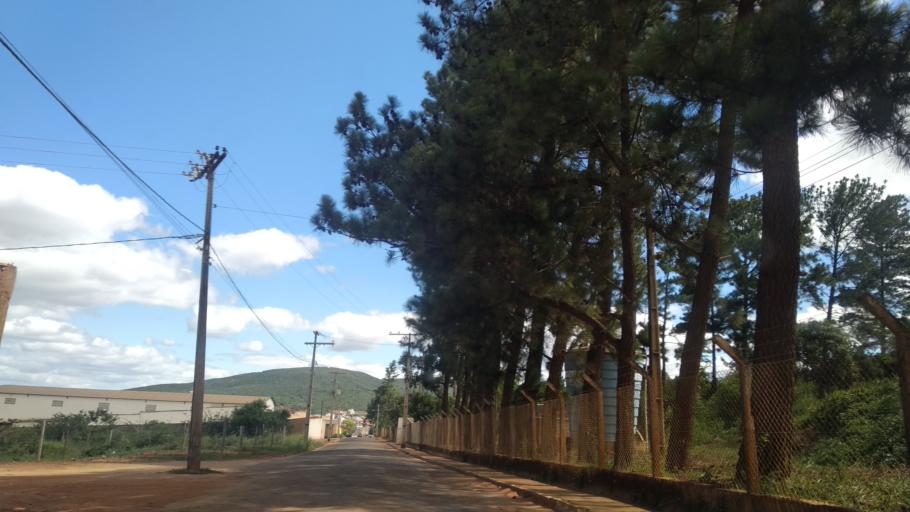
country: BR
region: Bahia
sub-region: Caetite
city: Caetite
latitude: -14.0560
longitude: -42.4871
